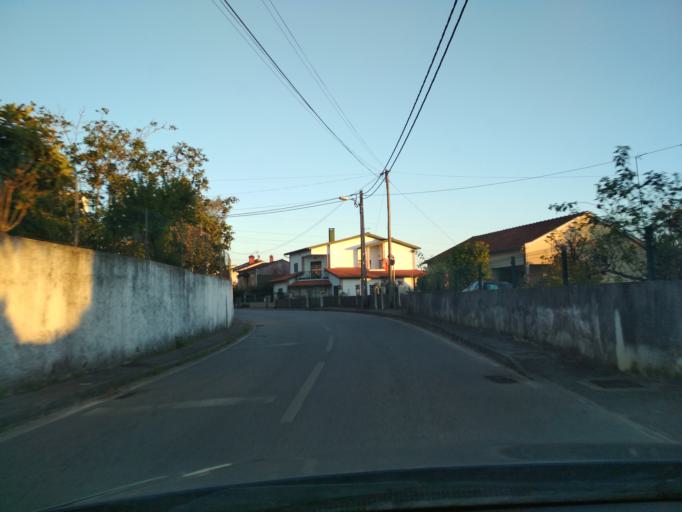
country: PT
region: Coimbra
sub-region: Condeixa-A-Nova
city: Condeixa-a-Nova
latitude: 40.1730
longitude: -8.4820
